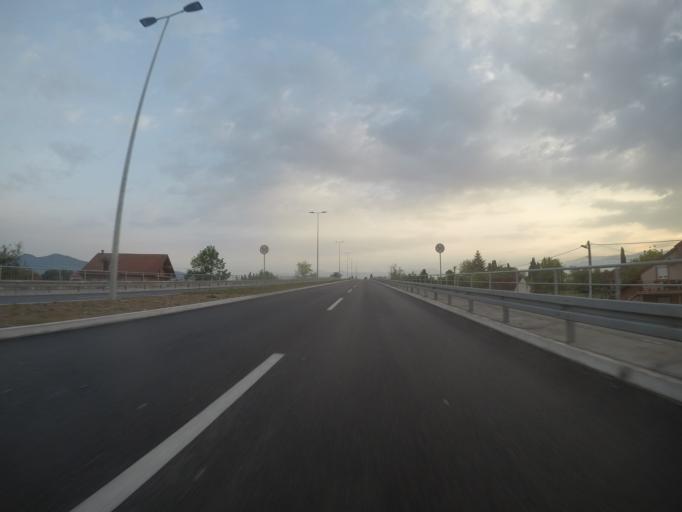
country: ME
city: Mojanovici
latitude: 42.3469
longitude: 19.2222
